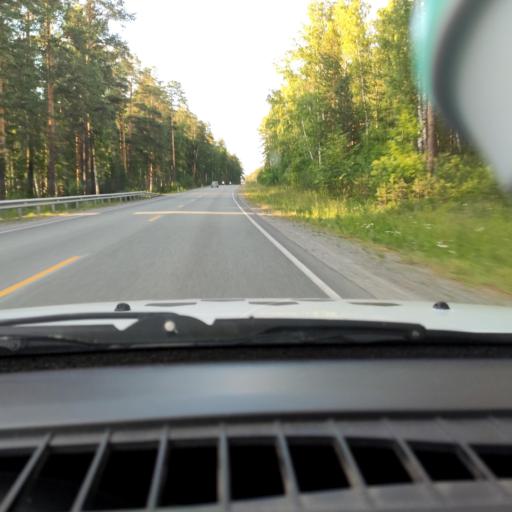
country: RU
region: Chelyabinsk
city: Karabash
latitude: 55.3093
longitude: 60.2080
